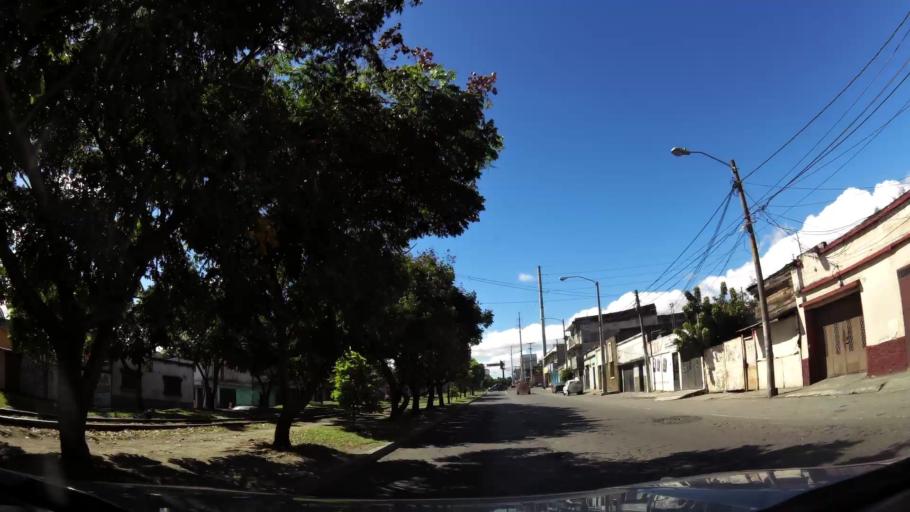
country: GT
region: Guatemala
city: Guatemala City
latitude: 14.6092
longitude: -90.5286
